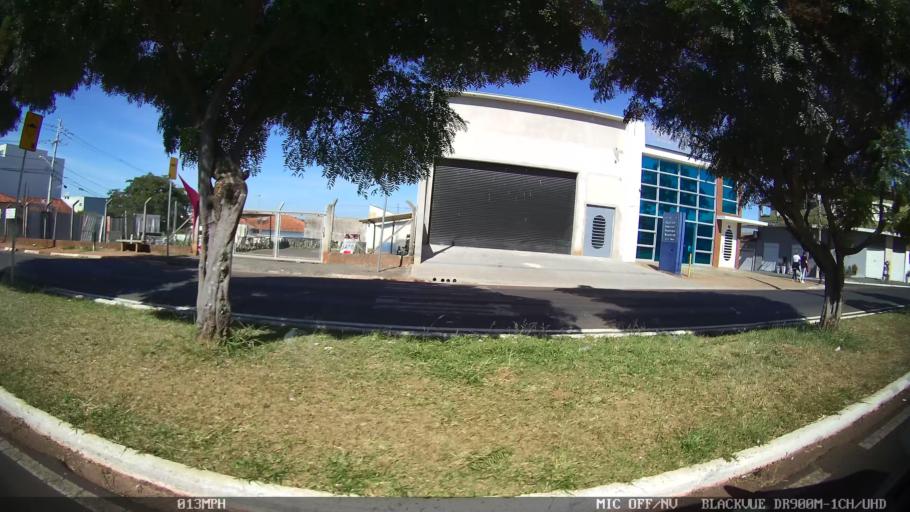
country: BR
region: Sao Paulo
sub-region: Franca
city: Franca
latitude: -20.5439
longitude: -47.3808
